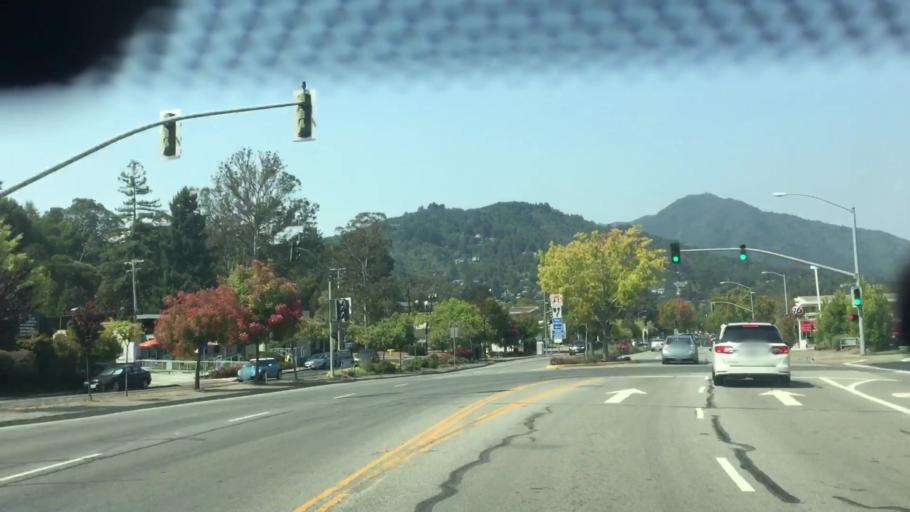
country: US
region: California
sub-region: Marin County
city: Corte Madera
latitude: 37.9251
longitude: -122.5172
